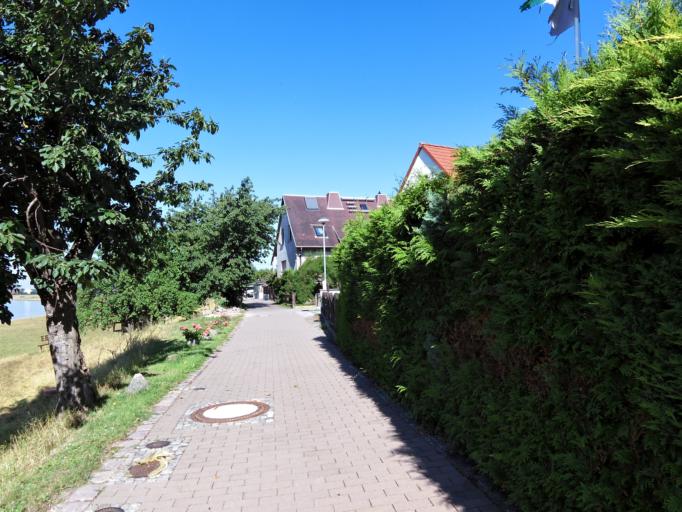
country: DE
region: Saxony
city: Riesa
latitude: 51.3466
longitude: 13.2834
